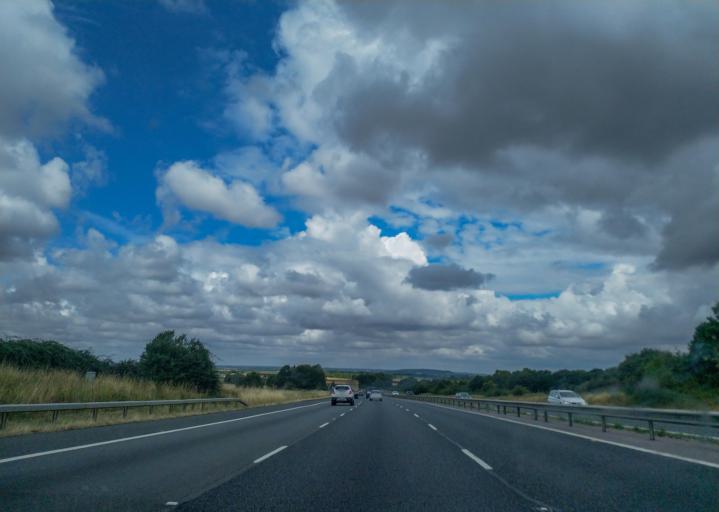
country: GB
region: England
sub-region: Oxfordshire
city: Wheatley
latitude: 51.8229
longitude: -1.1080
